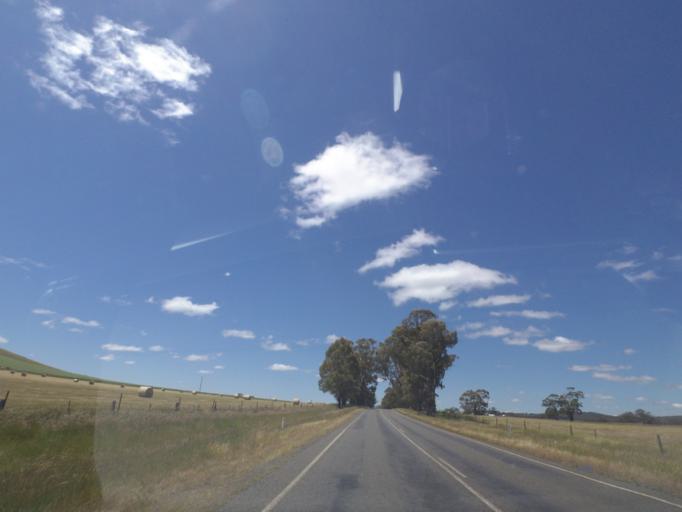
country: AU
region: Victoria
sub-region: Mount Alexander
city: Castlemaine
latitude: -37.3127
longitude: 144.2271
